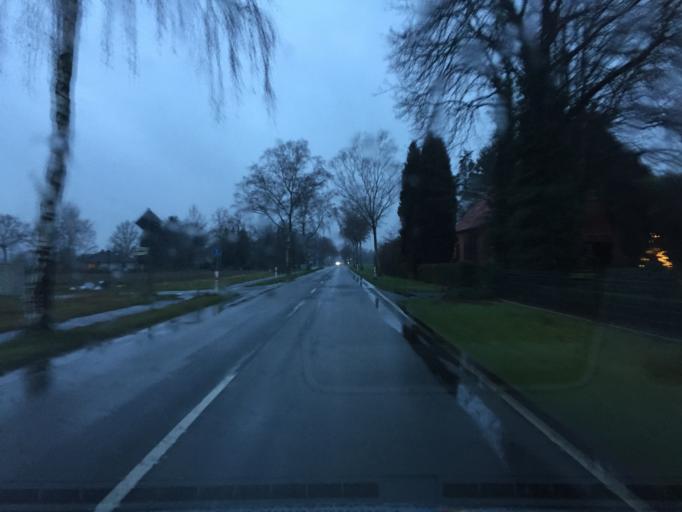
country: DE
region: Lower Saxony
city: Emtinghausen
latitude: 52.9406
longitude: 8.9921
